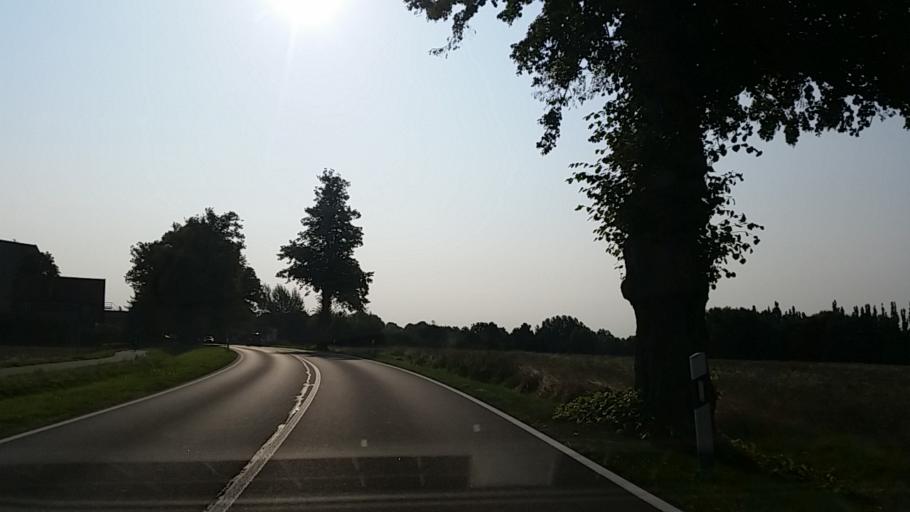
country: DE
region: Mecklenburg-Vorpommern
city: Hagenow
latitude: 53.4442
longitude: 11.1777
